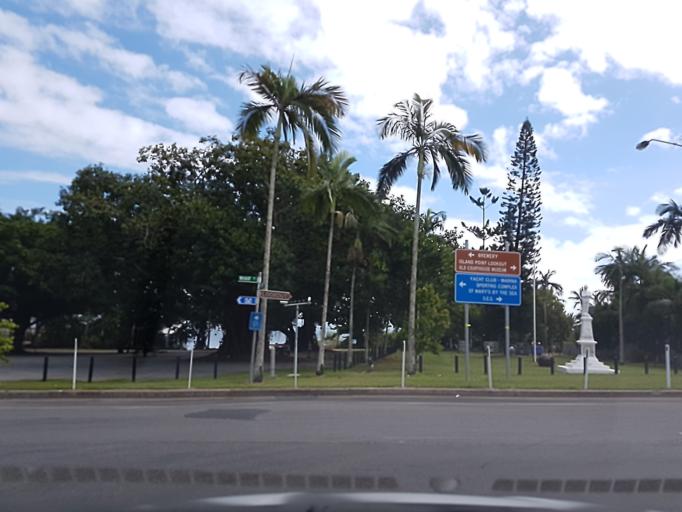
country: AU
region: Queensland
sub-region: Cairns
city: Port Douglas
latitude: -16.4806
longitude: 145.4624
